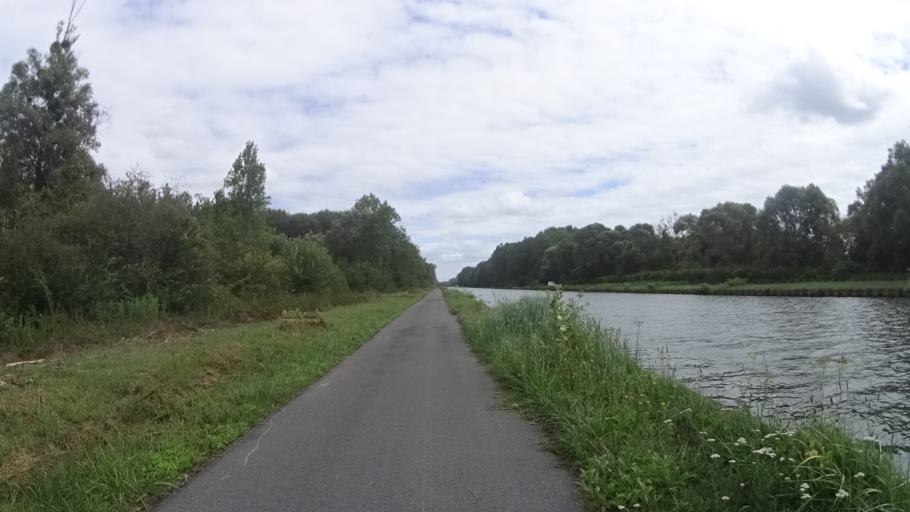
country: FR
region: Picardie
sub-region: Departement de l'Aisne
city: Blerancourt
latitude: 49.5786
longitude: 3.1231
